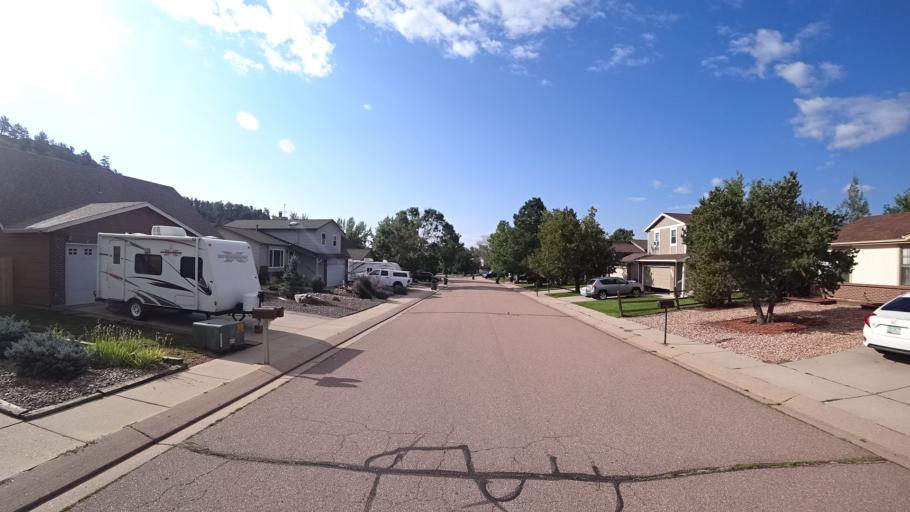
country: US
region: Colorado
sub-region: El Paso County
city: Air Force Academy
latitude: 38.9159
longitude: -104.8599
